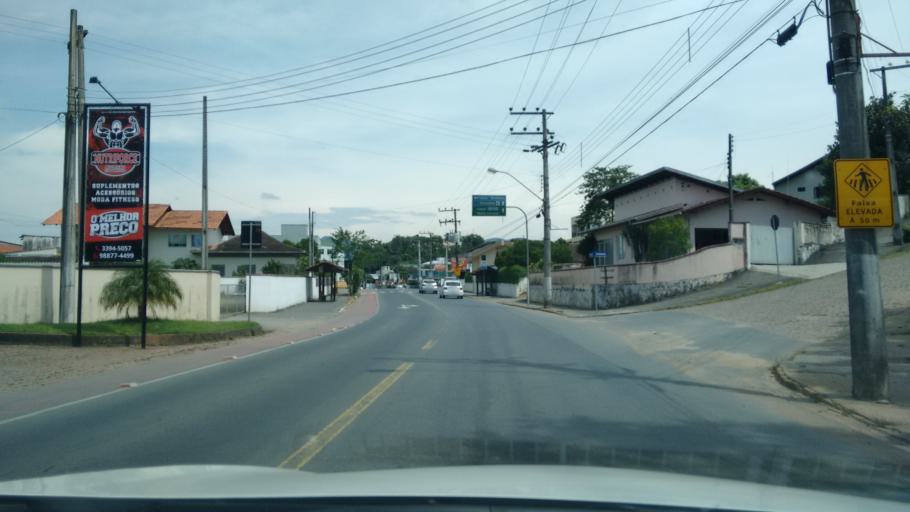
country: BR
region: Santa Catarina
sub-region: Timbo
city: Timbo
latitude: -26.8363
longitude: -49.2727
